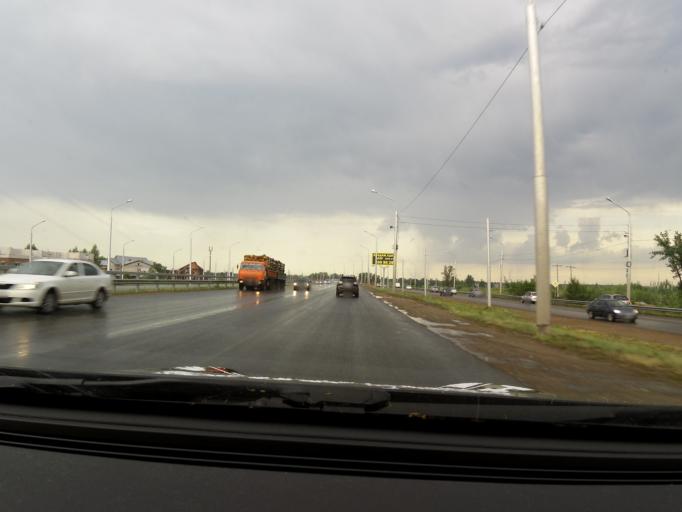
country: RU
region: Bashkortostan
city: Ufa
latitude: 54.7706
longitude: 55.9543
